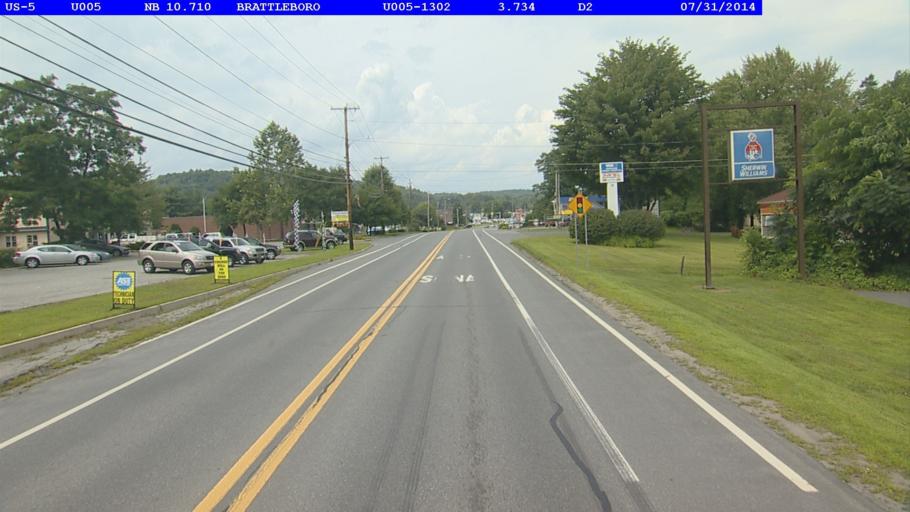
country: US
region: Vermont
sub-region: Windham County
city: Brattleboro
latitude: 42.8729
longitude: -72.5589
